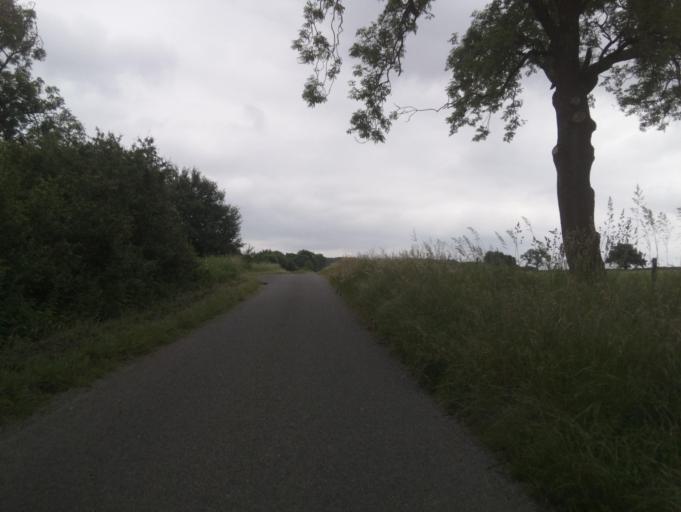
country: GB
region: England
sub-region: District of Rutland
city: Langham
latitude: 52.6761
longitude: -0.7929
